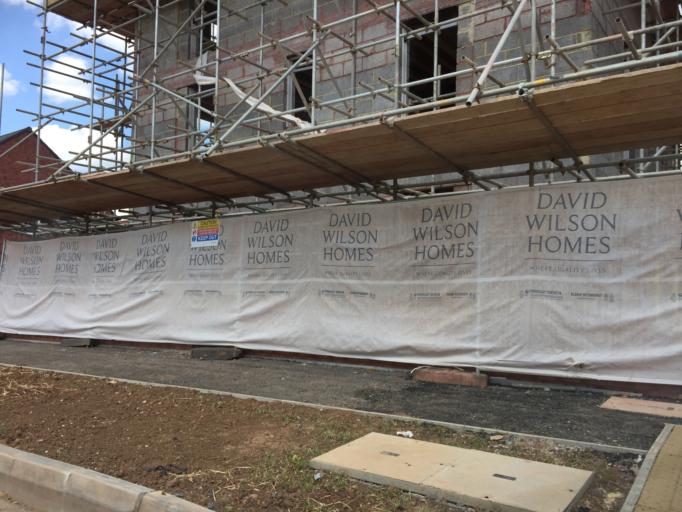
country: GB
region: England
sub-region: South Gloucestershire
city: Yate
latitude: 51.5583
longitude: -2.4146
